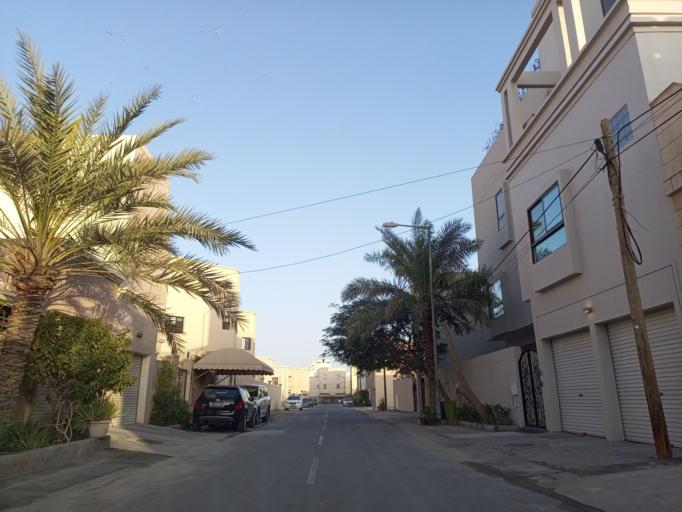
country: BH
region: Muharraq
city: Al Hadd
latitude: 26.2317
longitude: 50.6496
